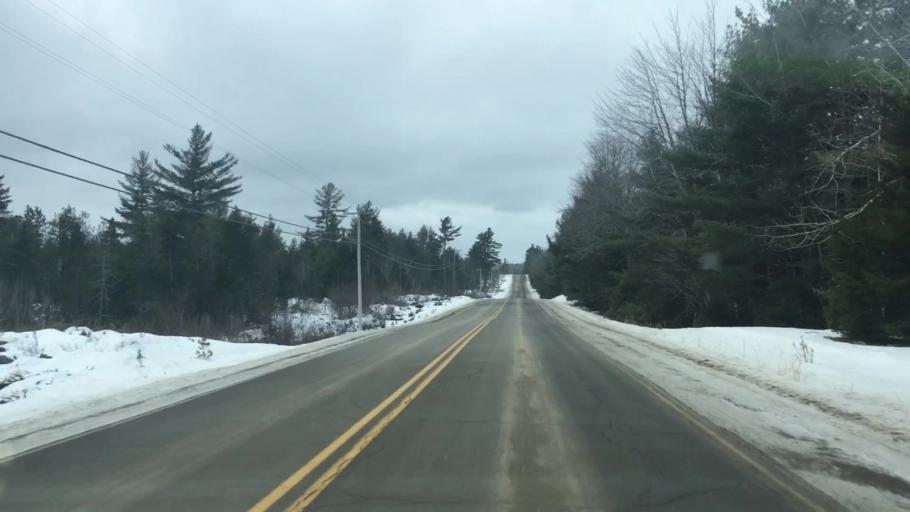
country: US
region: Maine
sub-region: Washington County
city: Calais
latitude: 45.0088
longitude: -67.4030
